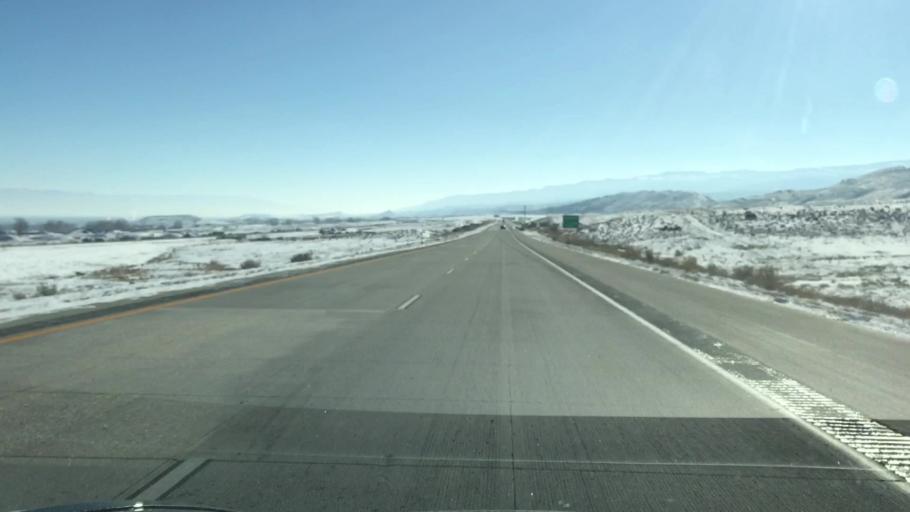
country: US
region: Colorado
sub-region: Mesa County
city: Loma
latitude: 39.1884
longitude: -108.8383
